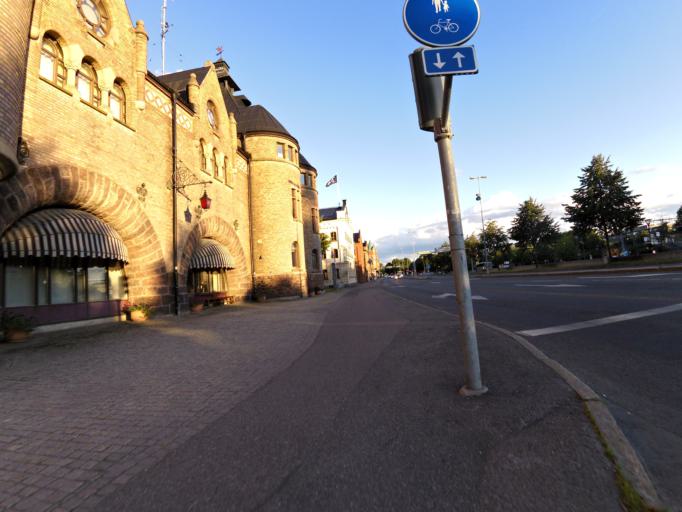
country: SE
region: Gaevleborg
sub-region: Gavle Kommun
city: Gavle
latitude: 60.6769
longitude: 17.1523
